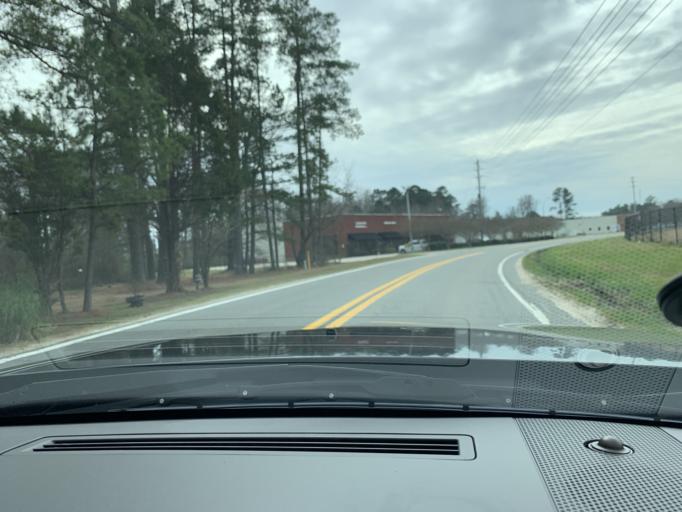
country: US
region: North Carolina
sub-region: Johnston County
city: Clayton
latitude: 35.6160
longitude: -78.4103
